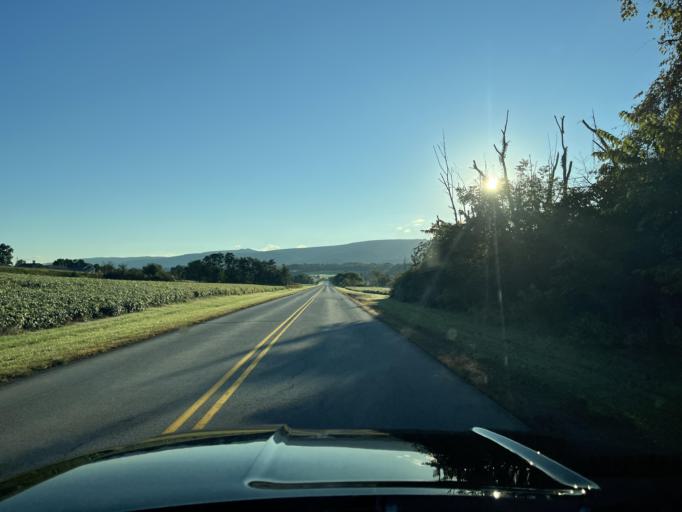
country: US
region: Pennsylvania
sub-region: Fayette County
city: Leith-Hatfield
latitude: 39.8660
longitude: -79.7368
